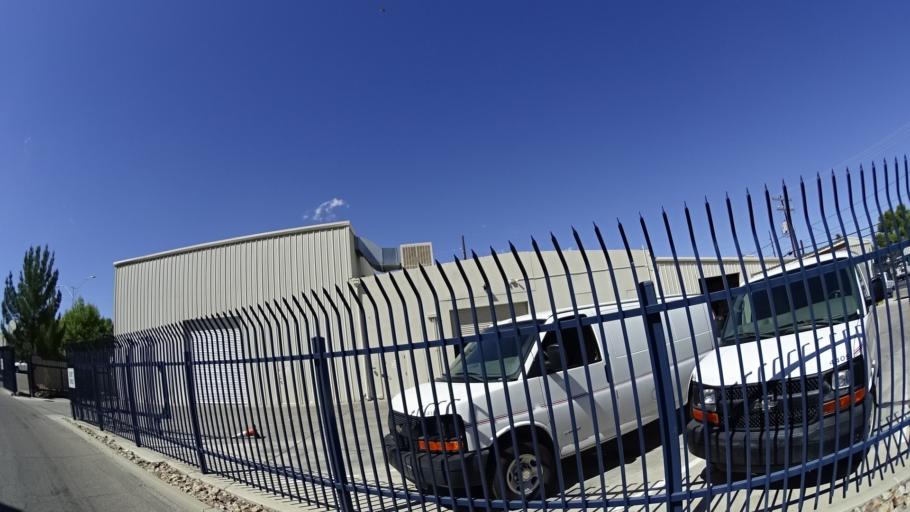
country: US
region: Arizona
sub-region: Pima County
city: Tucson
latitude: 32.2430
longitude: -110.9490
